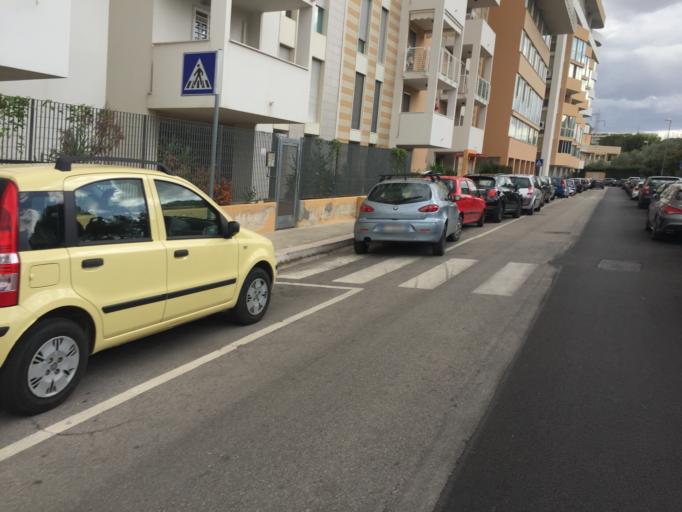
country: IT
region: Apulia
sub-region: Provincia di Bari
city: Bari
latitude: 41.1002
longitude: 16.8435
